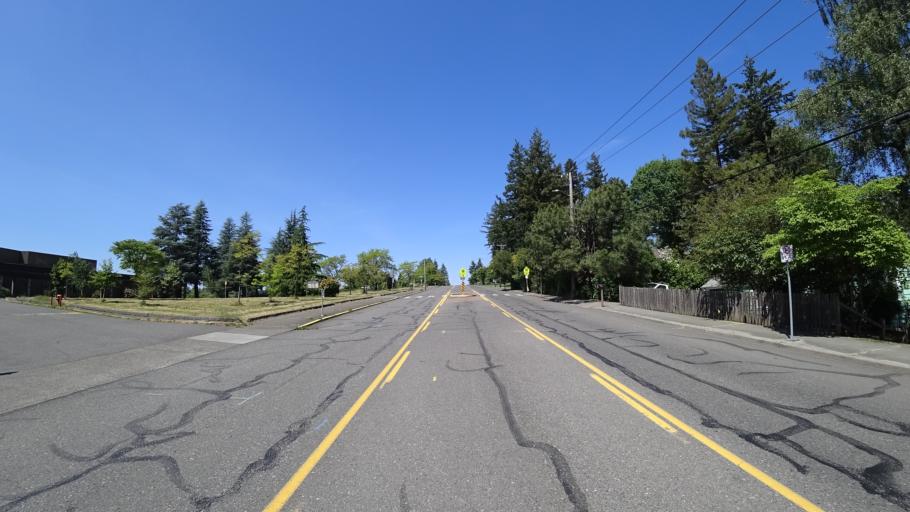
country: US
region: Oregon
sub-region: Washington County
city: Metzger
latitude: 45.4485
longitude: -122.7129
